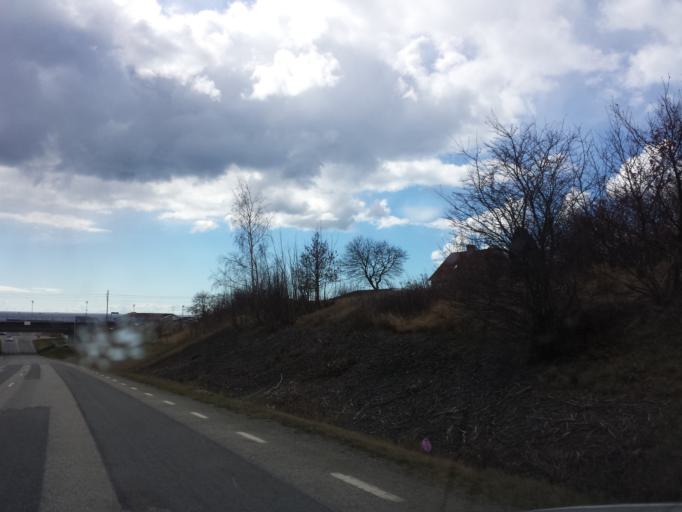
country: SE
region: Skane
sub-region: Ystads Kommun
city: Ystad
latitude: 55.4300
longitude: 13.7185
